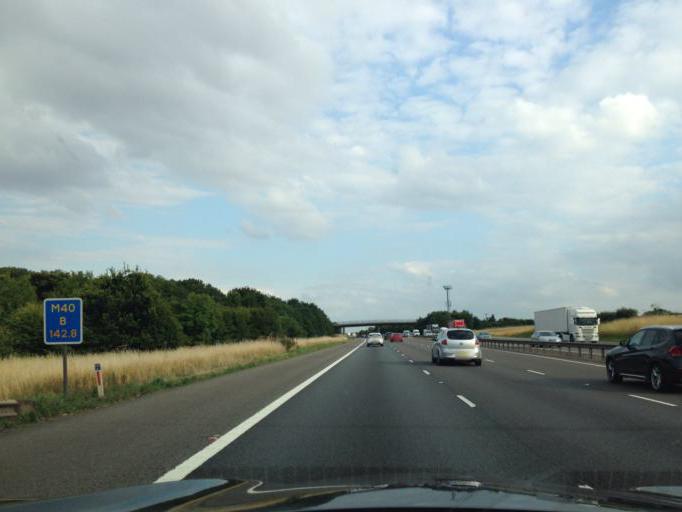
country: GB
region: England
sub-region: Warwickshire
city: Harbury
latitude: 52.2115
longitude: -1.4885
